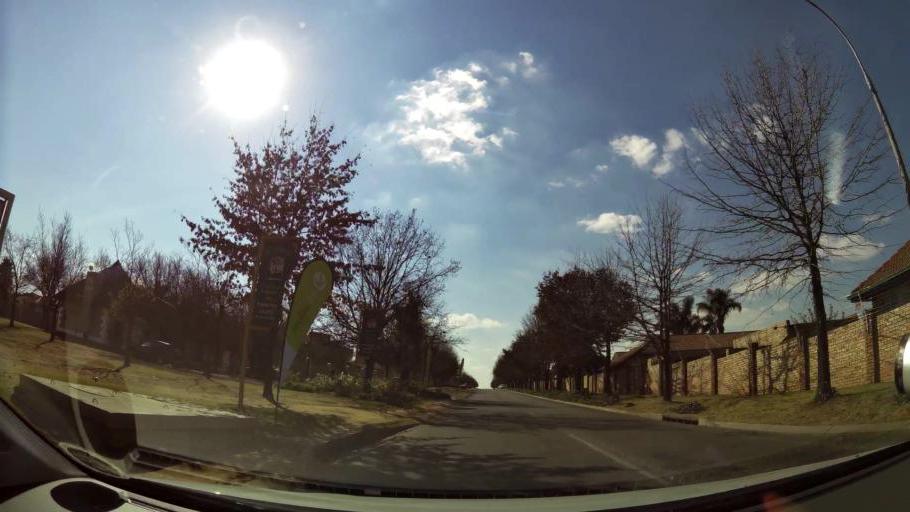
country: ZA
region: Gauteng
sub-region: Ekurhuleni Metropolitan Municipality
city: Tembisa
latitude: -26.0668
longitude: 28.2547
